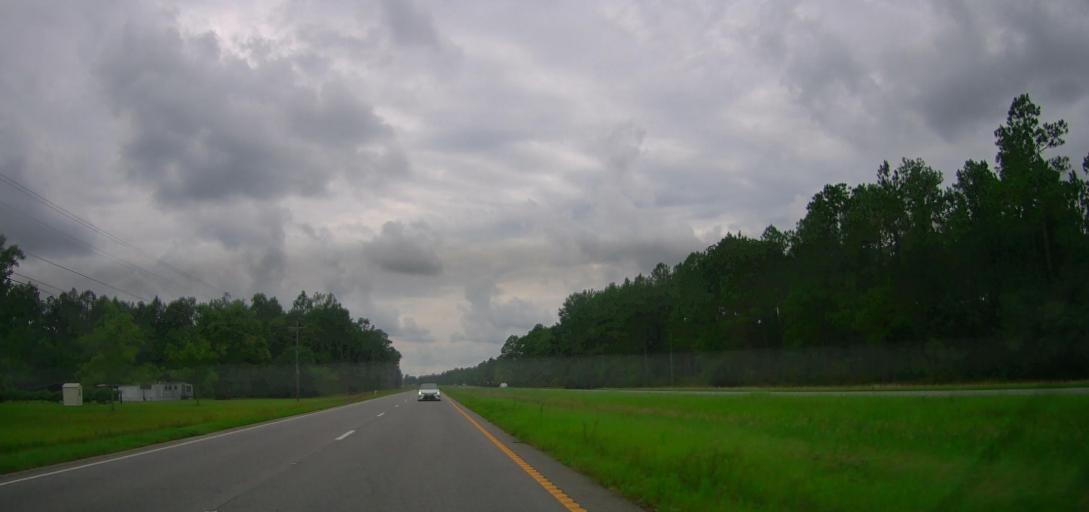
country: US
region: Georgia
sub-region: Appling County
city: Baxley
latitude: 31.8087
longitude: -82.4351
